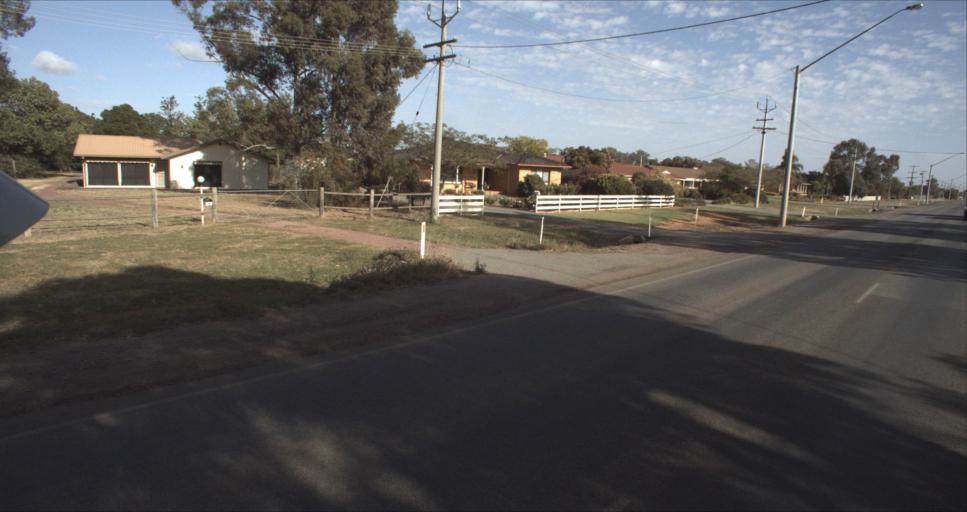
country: AU
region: New South Wales
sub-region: Leeton
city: Leeton
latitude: -34.5673
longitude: 146.3937
